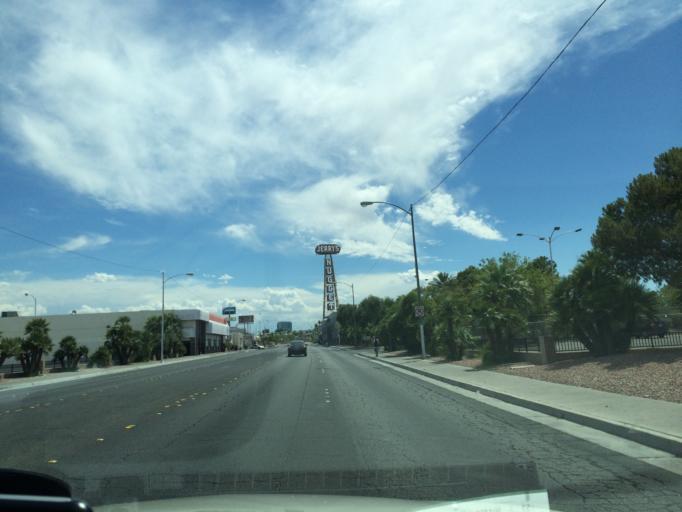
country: US
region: Nevada
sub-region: Clark County
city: North Las Vegas
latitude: 36.1944
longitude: -115.1307
